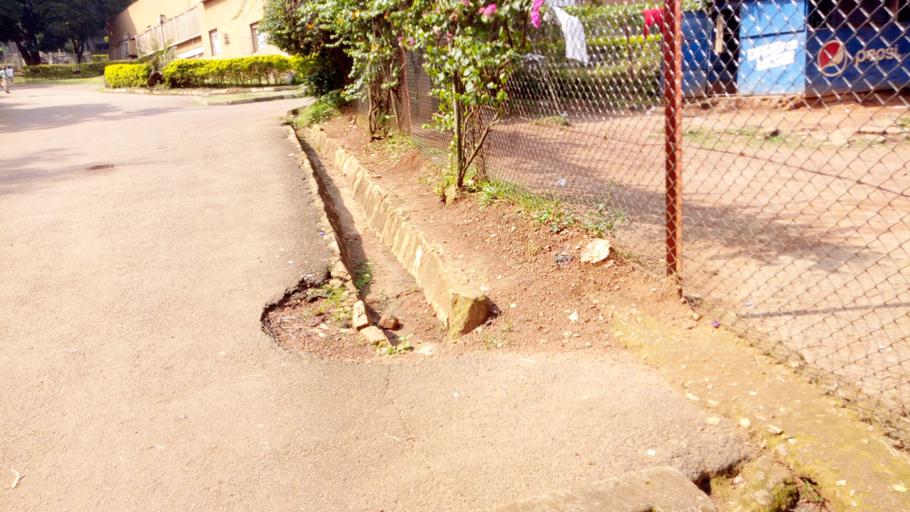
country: UG
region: Central Region
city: Kampala Central Division
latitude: 0.3290
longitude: 32.5673
